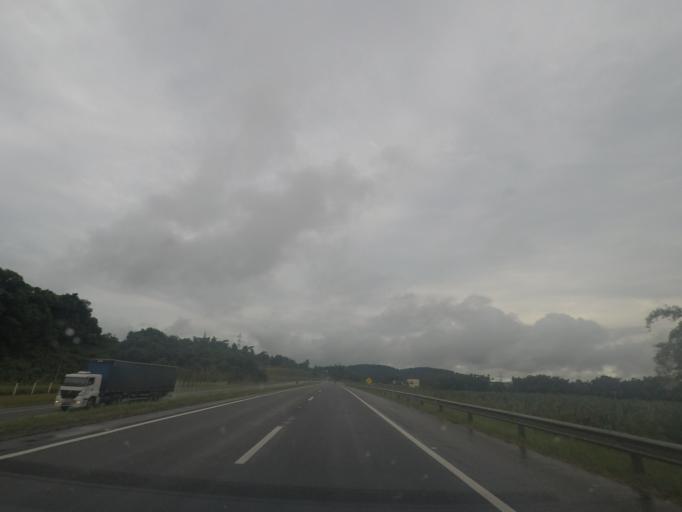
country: BR
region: Sao Paulo
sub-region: Jacupiranga
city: Jacupiranga
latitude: -24.6743
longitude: -47.9797
